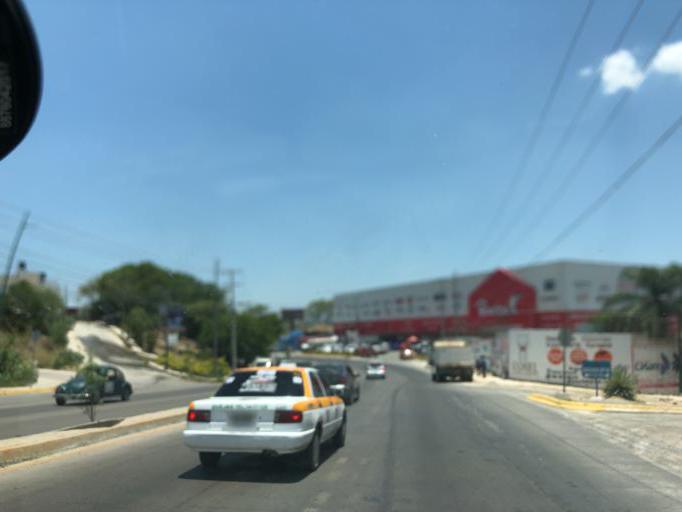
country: MX
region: Chiapas
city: Tuxtla Gutierrez
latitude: 16.7490
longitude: -93.1466
